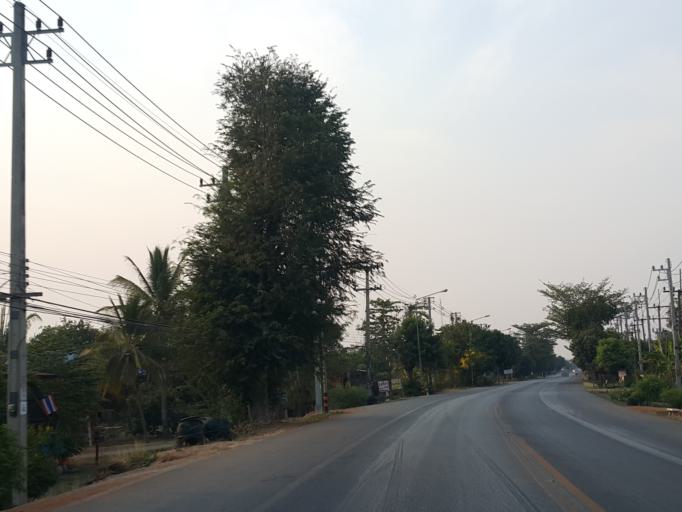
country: TH
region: Sukhothai
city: Si Samrong
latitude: 17.2290
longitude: 99.8583
